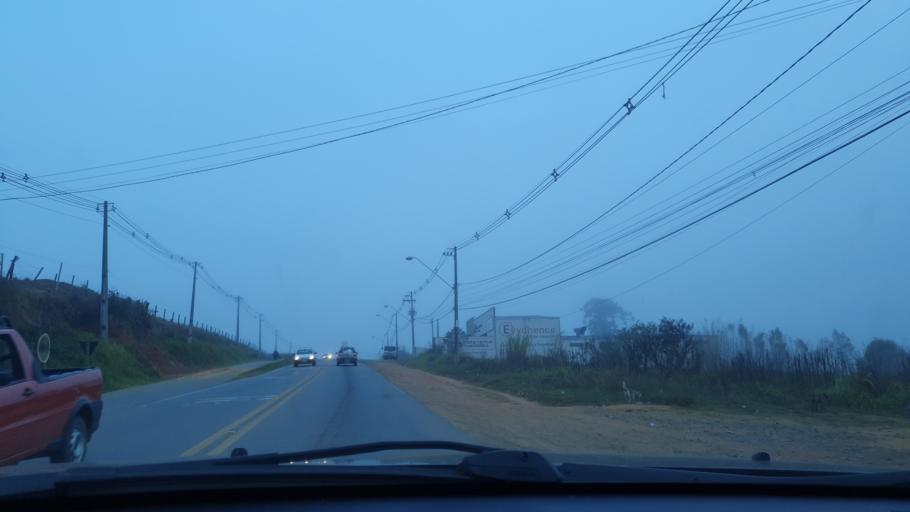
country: BR
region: Sao Paulo
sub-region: Ibiuna
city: Ibiuna
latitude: -23.6669
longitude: -47.2275
